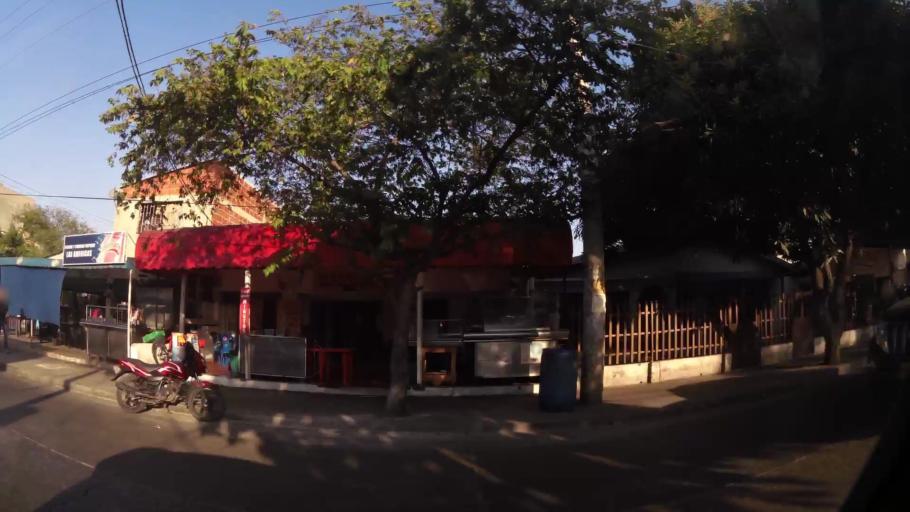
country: CO
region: Bolivar
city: Cartagena
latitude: 10.4481
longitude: -75.5173
